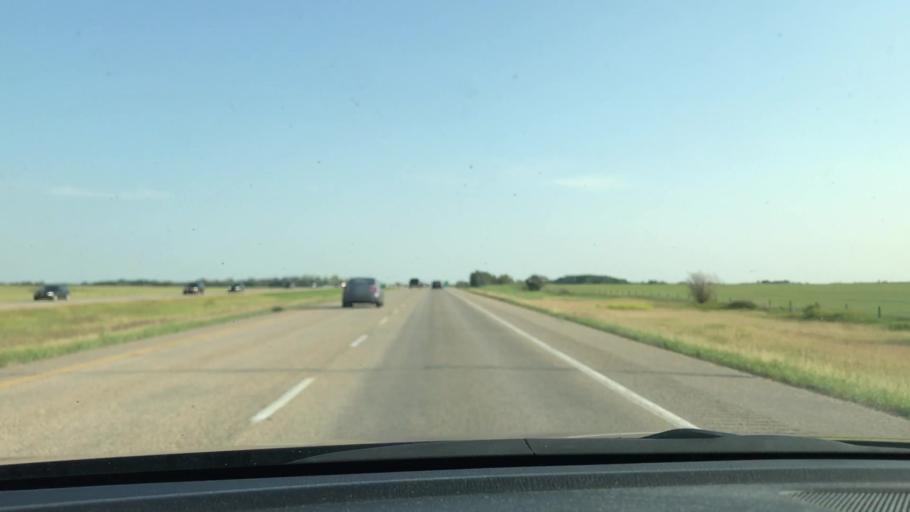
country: CA
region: Alberta
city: Millet
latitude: 53.1085
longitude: -113.5984
